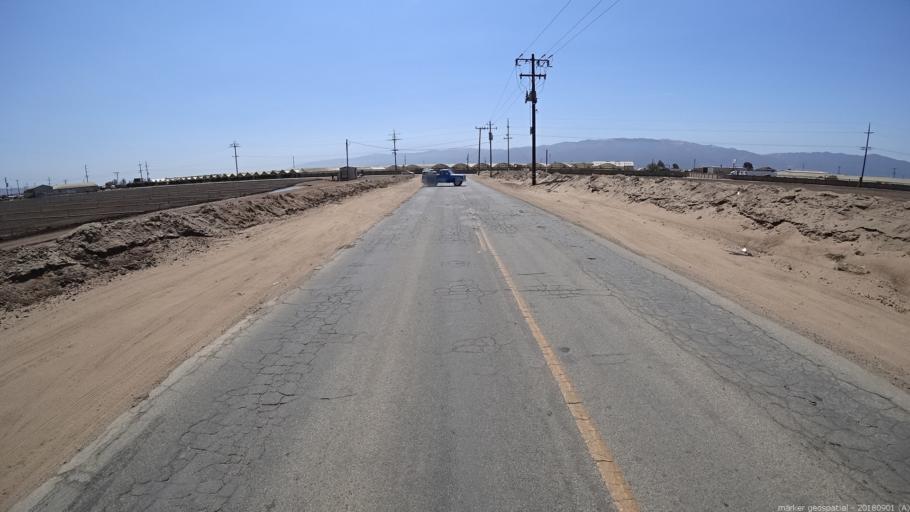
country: US
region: California
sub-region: Monterey County
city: Chualar
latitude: 36.6319
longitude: -121.5427
